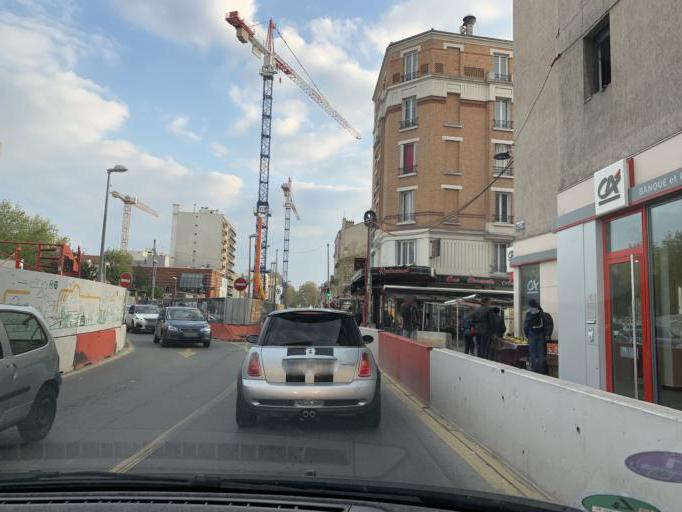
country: FR
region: Ile-de-France
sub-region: Departement de Seine-Saint-Denis
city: Aubervilliers
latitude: 48.9143
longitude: 2.3809
